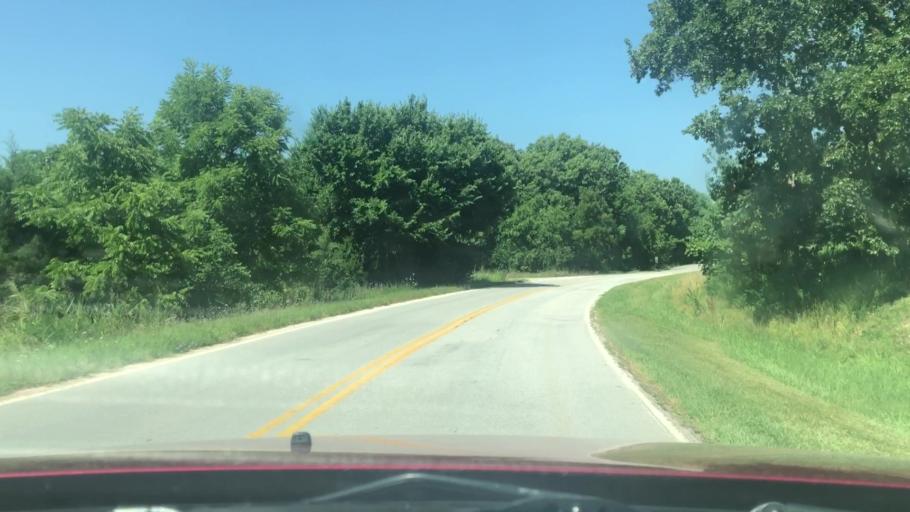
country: US
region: Missouri
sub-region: Greene County
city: Springfield
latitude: 37.2726
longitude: -93.2180
